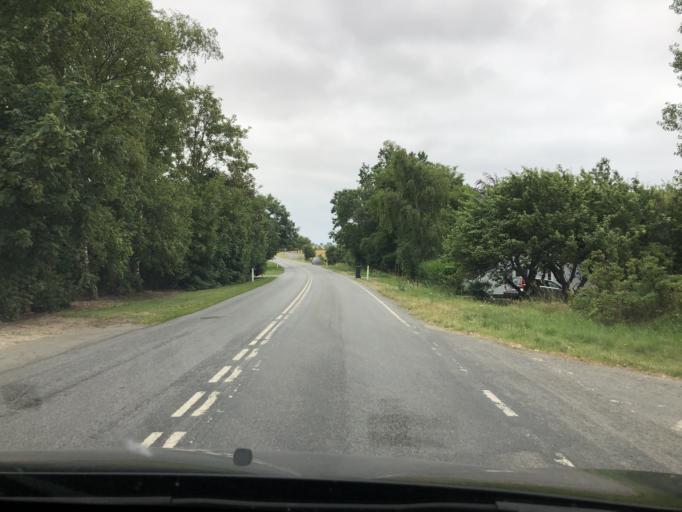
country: DK
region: South Denmark
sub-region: AEro Kommune
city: AEroskobing
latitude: 54.9326
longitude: 10.2646
